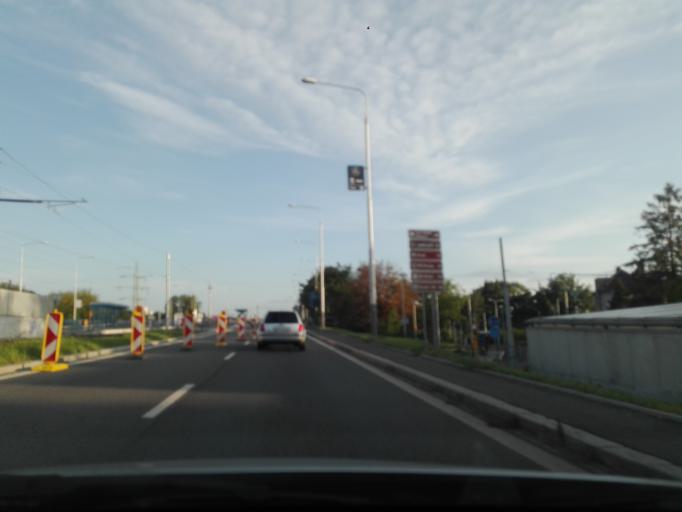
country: CZ
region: Moravskoslezsky
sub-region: Okres Ostrava-Mesto
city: Ostrava
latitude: 49.7961
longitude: 18.2492
